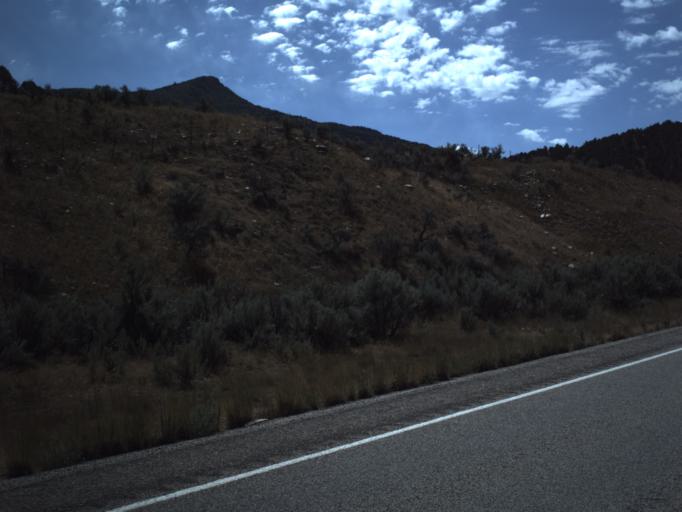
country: US
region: Utah
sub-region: Utah County
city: Woodland Hills
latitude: 39.9456
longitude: -111.5398
